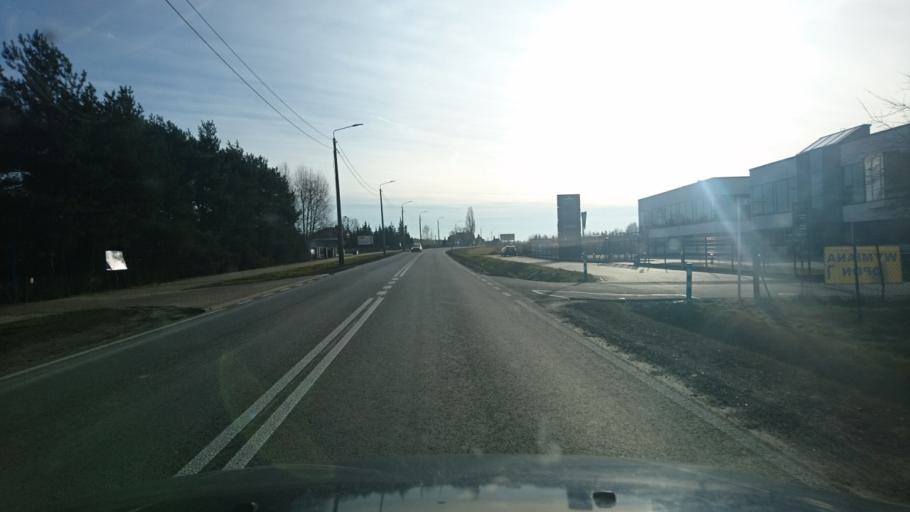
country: PL
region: Greater Poland Voivodeship
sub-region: Powiat ostrzeszowski
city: Ostrzeszow
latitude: 51.4436
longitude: 17.9127
